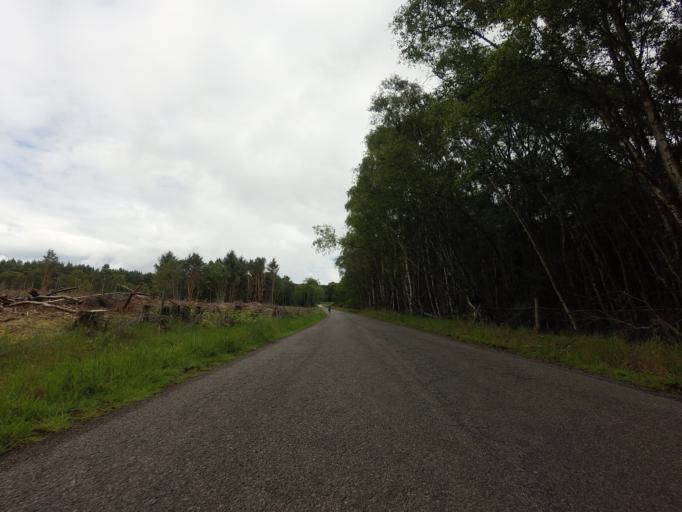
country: GB
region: Scotland
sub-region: Moray
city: Lhanbryd
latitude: 57.6649
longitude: -3.1745
